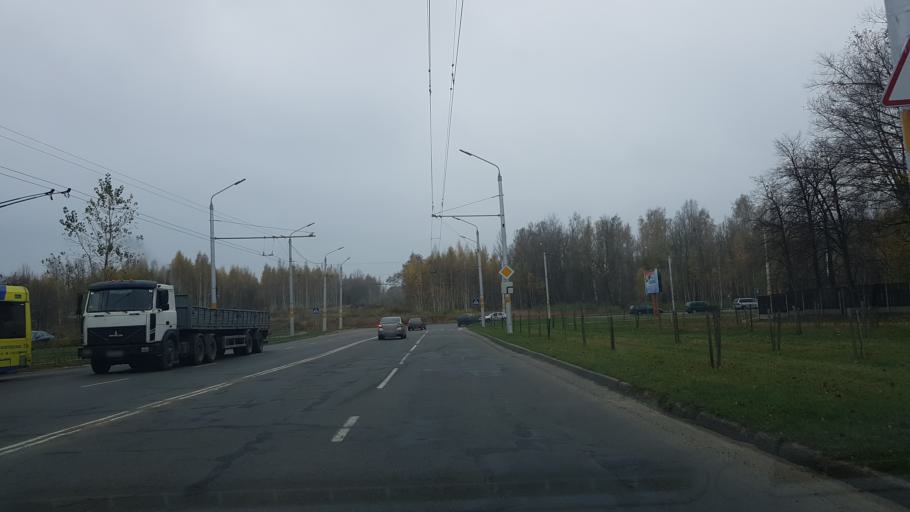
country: BY
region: Mogilev
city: Babruysk
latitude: 53.1859
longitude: 29.2252
